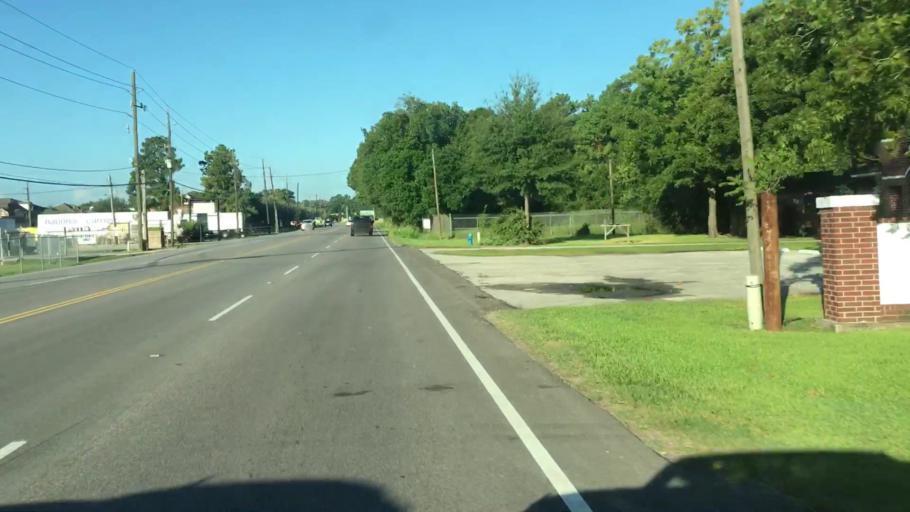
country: US
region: Texas
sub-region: Harris County
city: Humble
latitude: 29.9585
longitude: -95.2610
